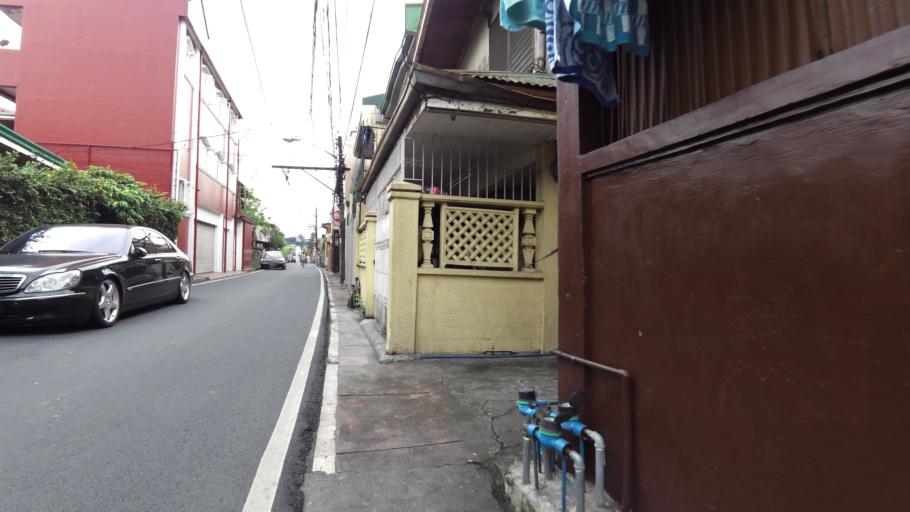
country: PH
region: Metro Manila
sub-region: Marikina
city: Calumpang
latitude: 14.6282
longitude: 121.0973
